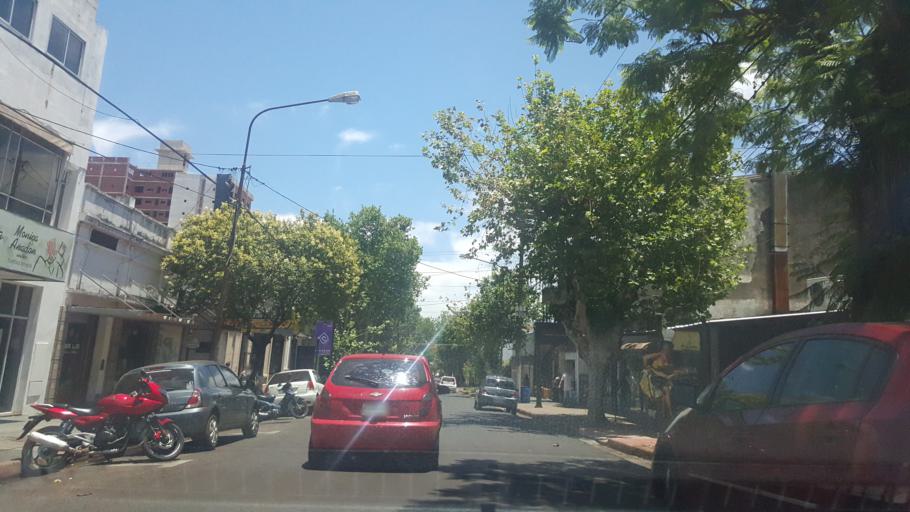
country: AR
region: Misiones
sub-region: Departamento de Capital
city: Posadas
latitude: -27.3650
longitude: -55.8954
